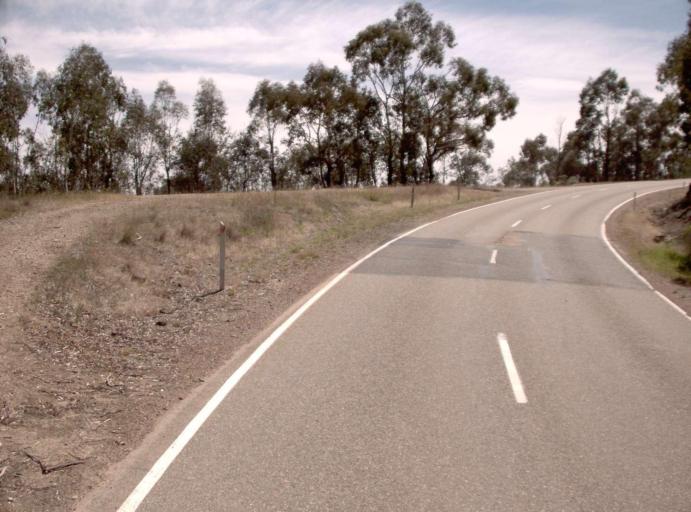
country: AU
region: Victoria
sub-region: Alpine
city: Mount Beauty
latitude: -37.0423
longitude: 147.6231
